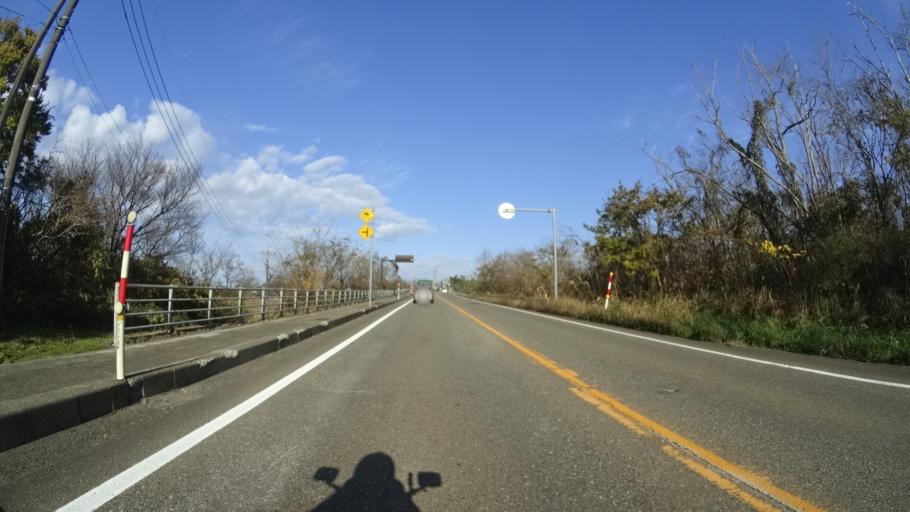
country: JP
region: Niigata
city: Joetsu
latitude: 37.2620
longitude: 138.3721
